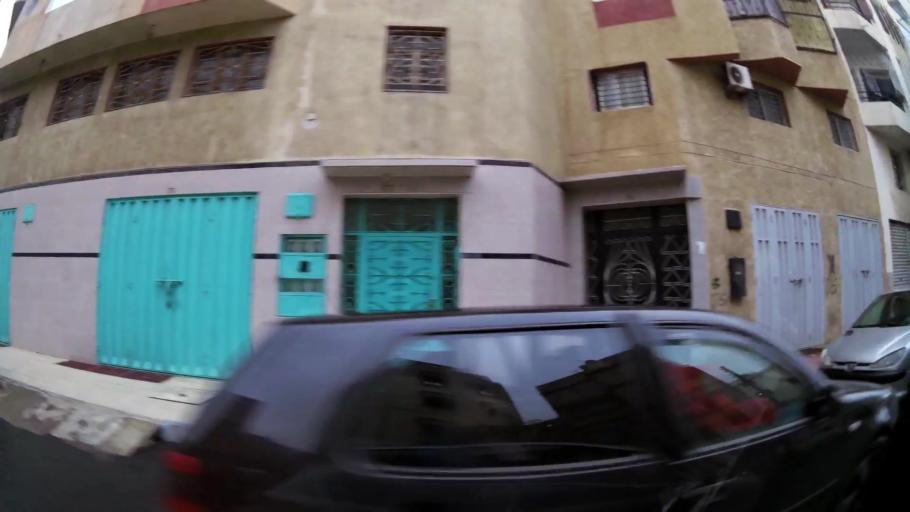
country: MA
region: Grand Casablanca
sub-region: Casablanca
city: Casablanca
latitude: 33.5560
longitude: -7.5849
